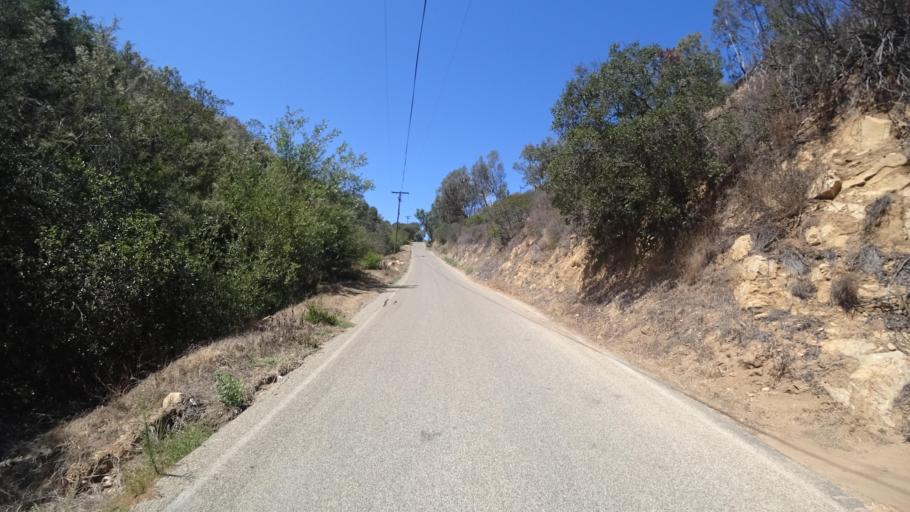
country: US
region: California
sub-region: San Diego County
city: Rainbow
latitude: 33.3849
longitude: -117.1202
